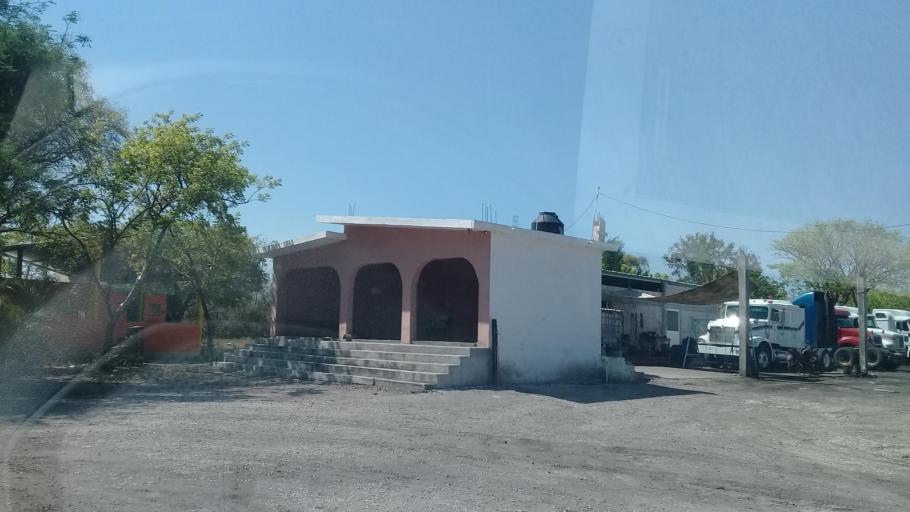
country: MX
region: Veracruz
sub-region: Emiliano Zapata
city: Plan del Rio
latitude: 19.3933
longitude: -96.6211
